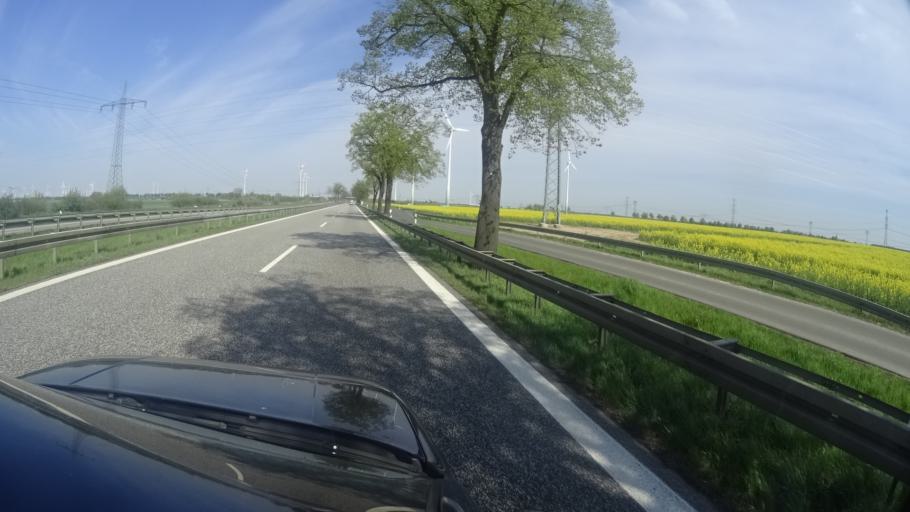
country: DE
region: Brandenburg
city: Wustermark
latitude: 52.5735
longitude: 12.9122
